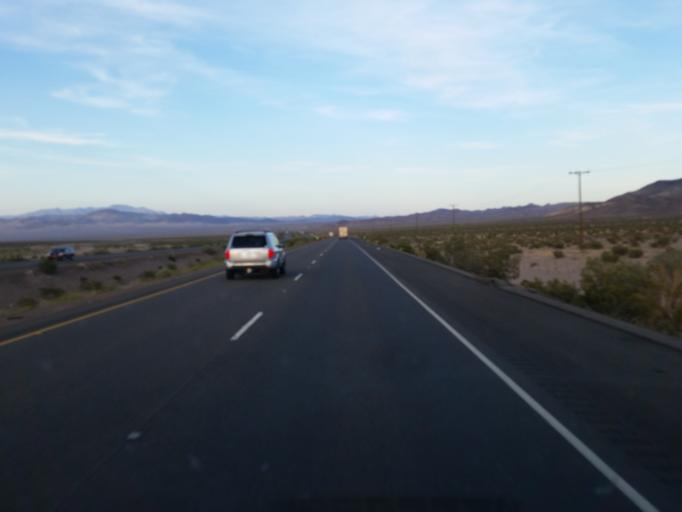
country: US
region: California
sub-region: San Bernardino County
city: Joshua Tree
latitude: 34.7269
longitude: -116.2482
